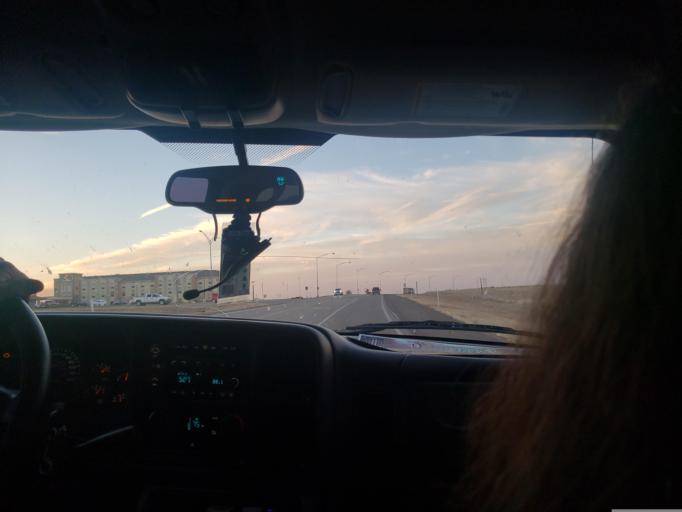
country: US
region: Kansas
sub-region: Seward County
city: Liberal
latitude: 37.0716
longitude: -100.9192
